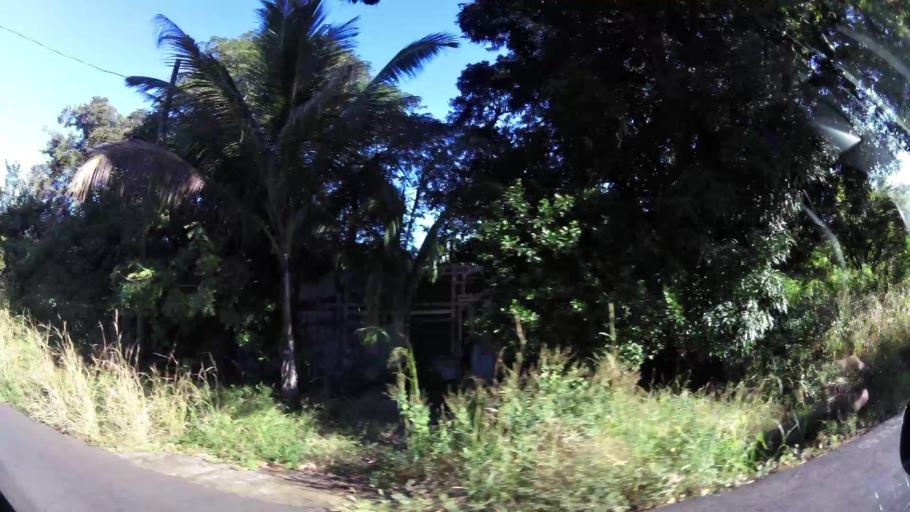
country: CR
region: Guanacaste
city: Sardinal
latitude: 10.4995
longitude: -85.6415
